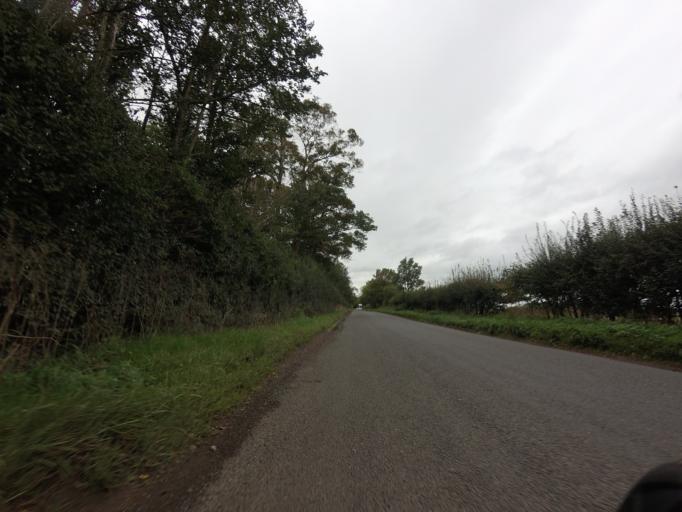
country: GB
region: England
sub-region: Cambridgeshire
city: Melbourn
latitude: 52.1062
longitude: 0.0472
